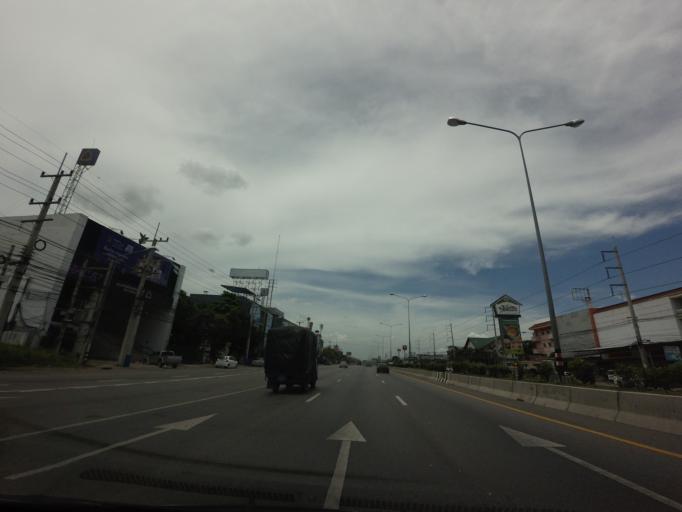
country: TH
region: Phetchaburi
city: Phetchaburi
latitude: 13.1085
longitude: 99.9333
